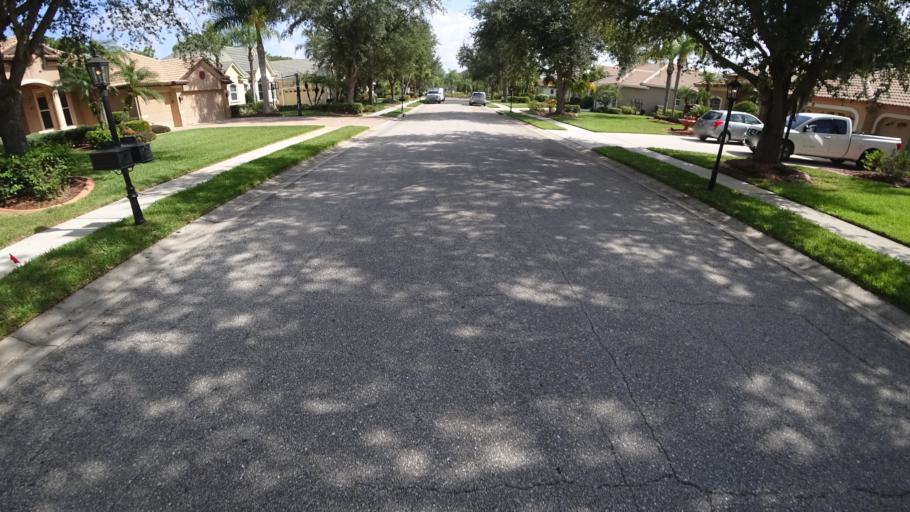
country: US
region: Florida
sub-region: Sarasota County
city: The Meadows
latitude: 27.4032
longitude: -82.4463
